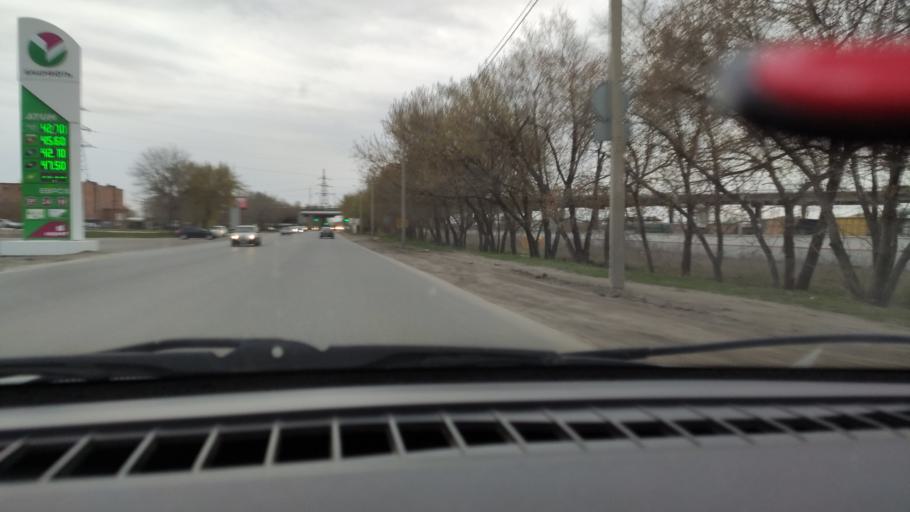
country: RU
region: Orenburg
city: Orenburg
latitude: 51.8314
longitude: 55.1092
